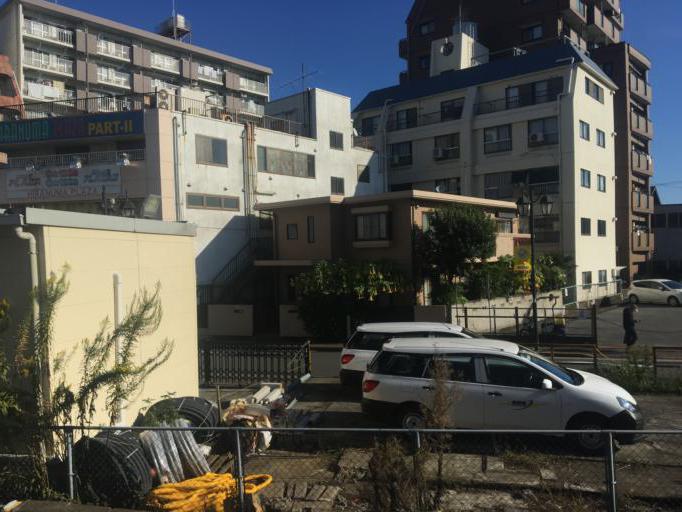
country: JP
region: Chiba
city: Matsudo
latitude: 35.7419
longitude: 139.8844
